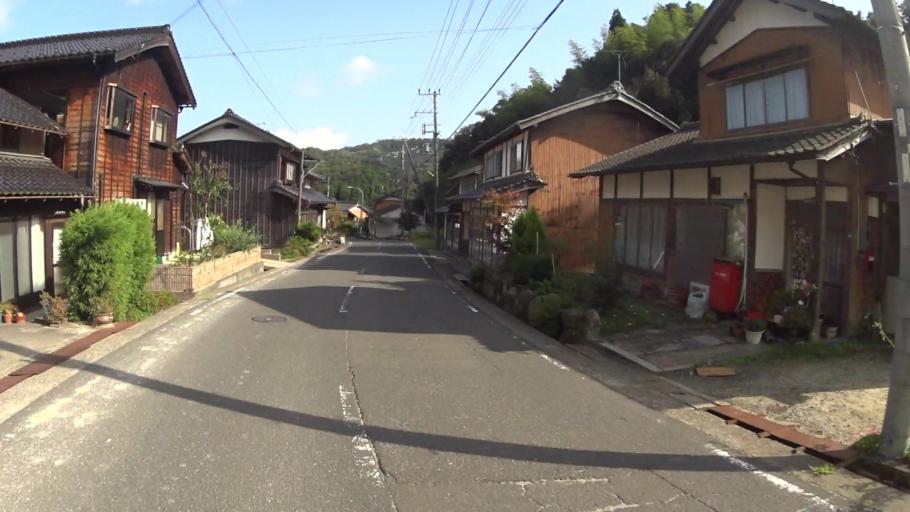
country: JP
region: Kyoto
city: Miyazu
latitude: 35.5719
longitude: 135.1146
